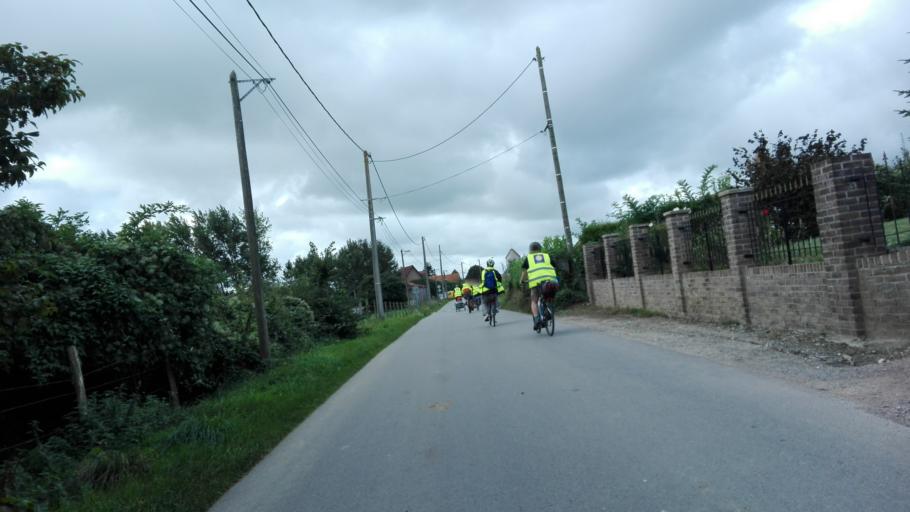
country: FR
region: Nord-Pas-de-Calais
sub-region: Departement du Pas-de-Calais
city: Tournehem-sur-la-Hem
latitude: 50.7949
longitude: 1.9992
